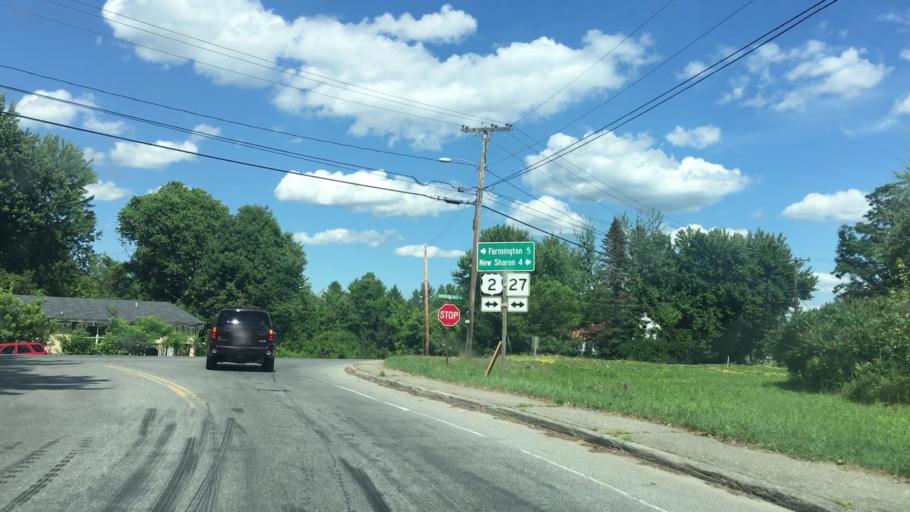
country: US
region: Maine
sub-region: Franklin County
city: New Sharon
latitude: 44.6215
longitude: -70.0724
